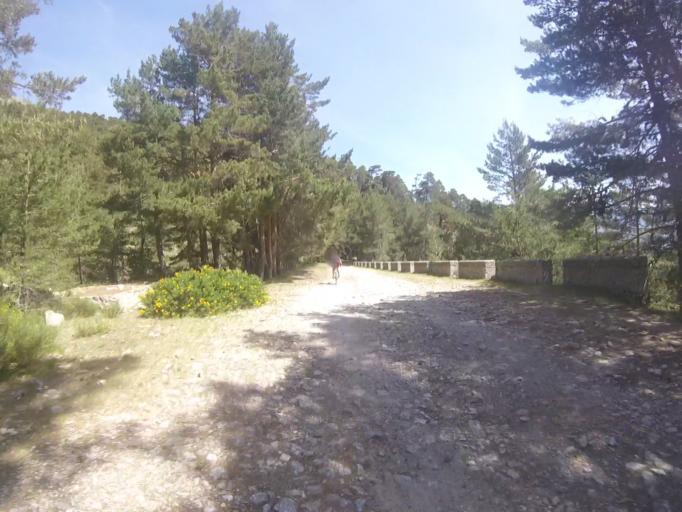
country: ES
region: Madrid
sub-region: Provincia de Madrid
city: Cercedilla
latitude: 40.7961
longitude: -4.0636
